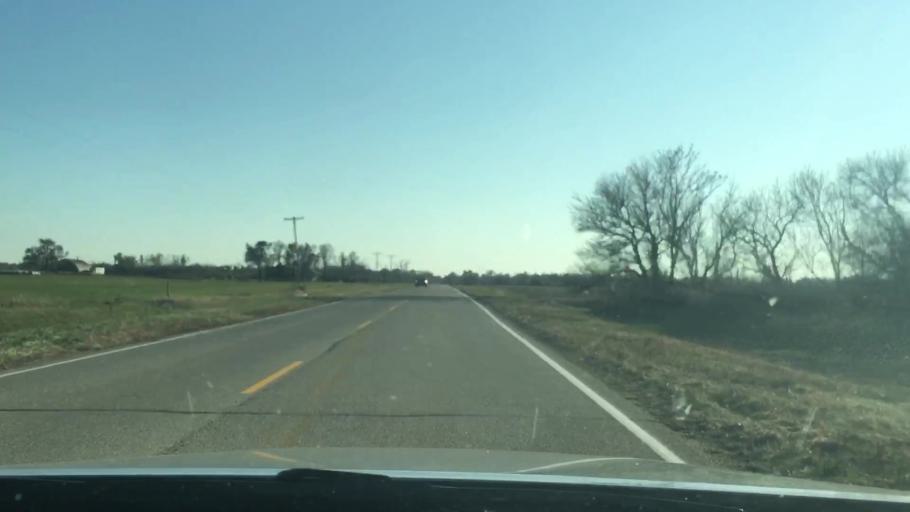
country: US
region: Kansas
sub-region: Reno County
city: Nickerson
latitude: 38.1670
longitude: -98.0876
